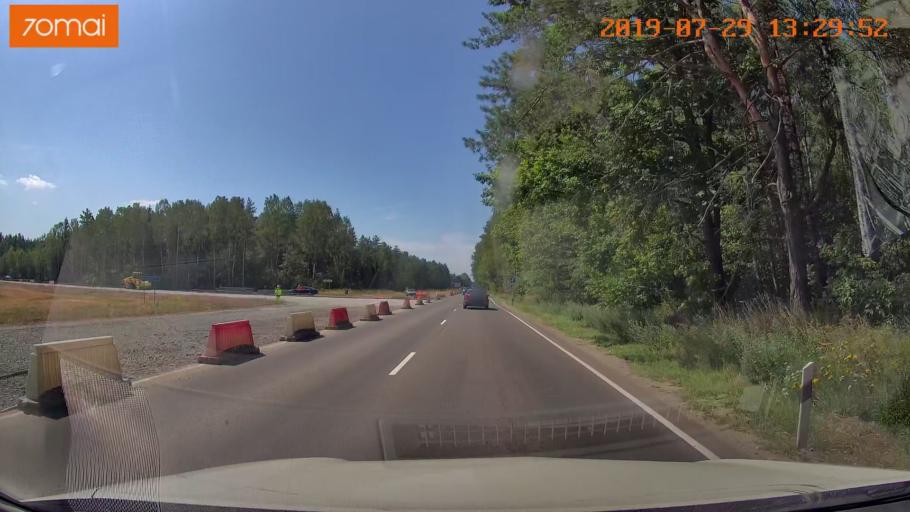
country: RU
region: Kaliningrad
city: Vzmorye
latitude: 54.7010
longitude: 20.2623
